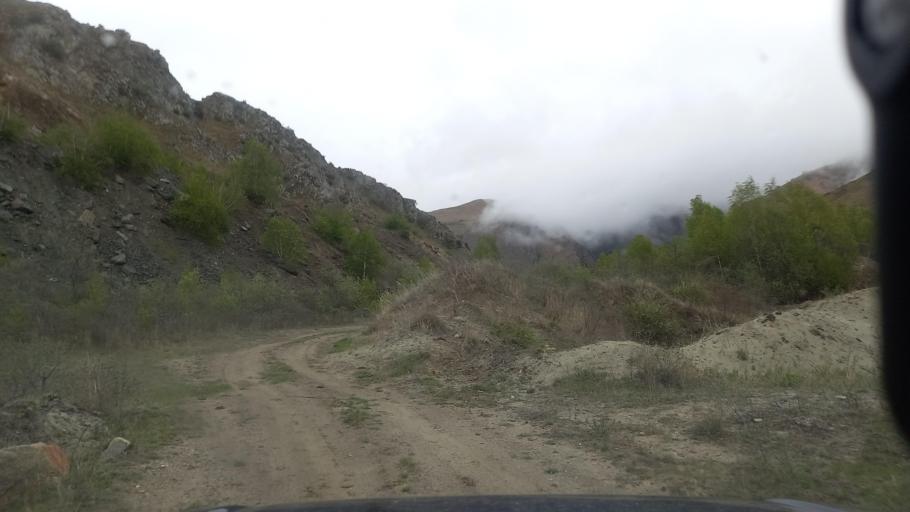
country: RU
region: Kabardino-Balkariya
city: Bylym
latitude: 43.4553
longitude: 43.0000
